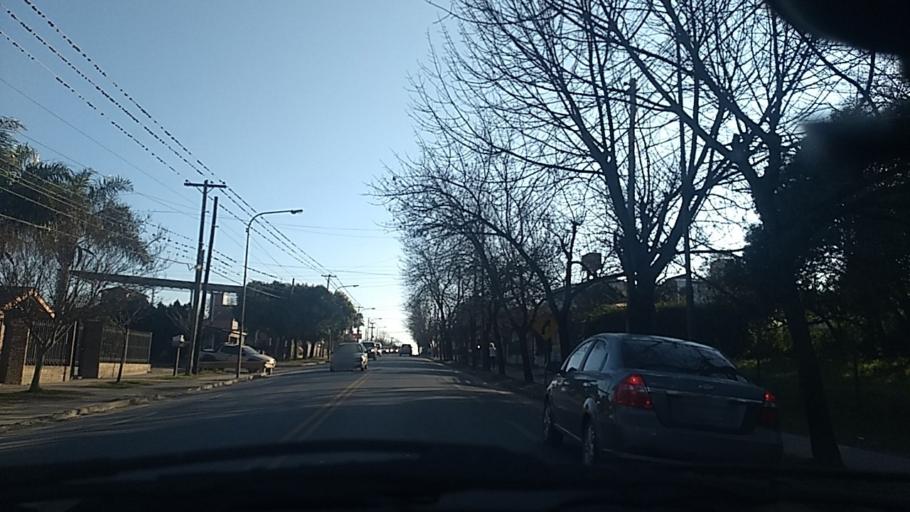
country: AR
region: Cordoba
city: Salsipuedes
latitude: -31.1342
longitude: -64.2959
